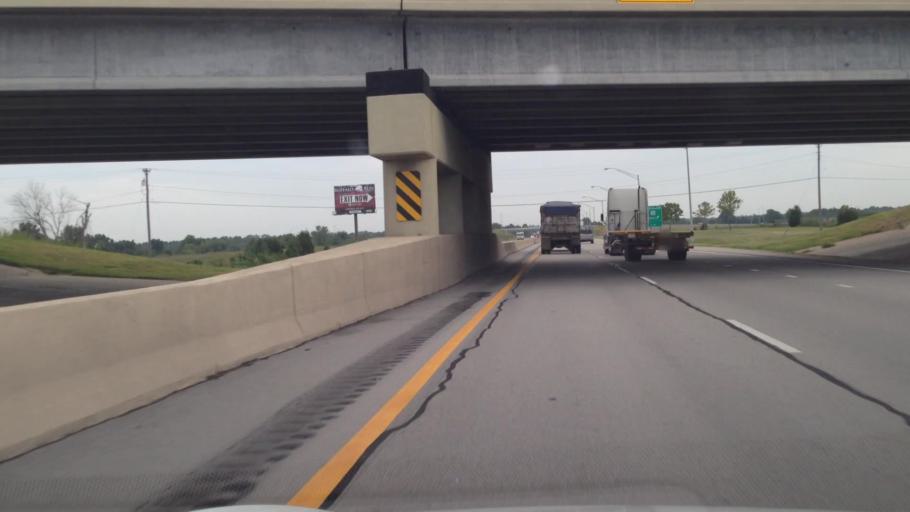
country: US
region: Oklahoma
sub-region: Ottawa County
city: Miami
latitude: 36.8713
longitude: -94.8473
